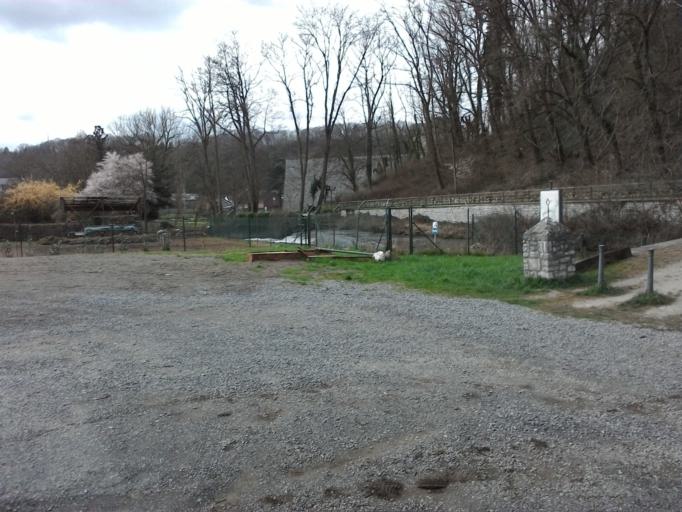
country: BE
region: Wallonia
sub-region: Province de Liege
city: Hamoir
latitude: 50.3776
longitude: 5.5270
